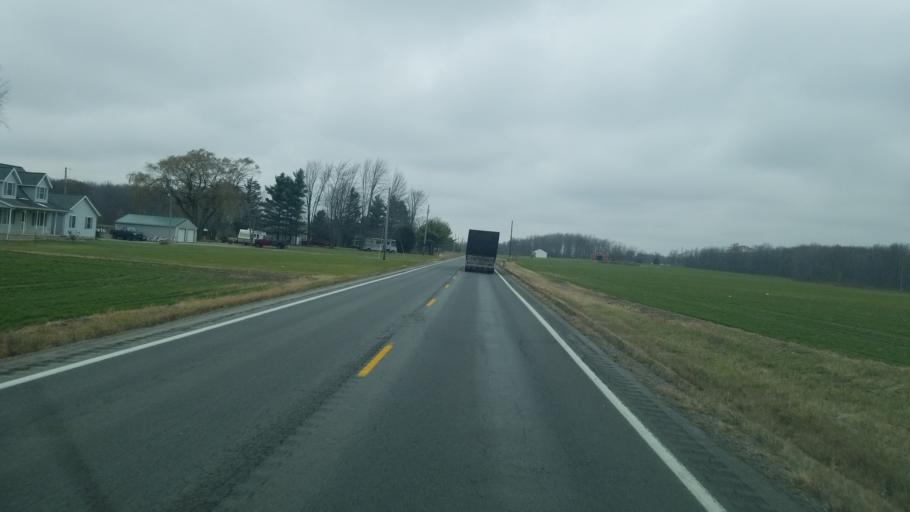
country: US
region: Ohio
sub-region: Huron County
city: Greenwich
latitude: 41.1099
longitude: -82.5017
